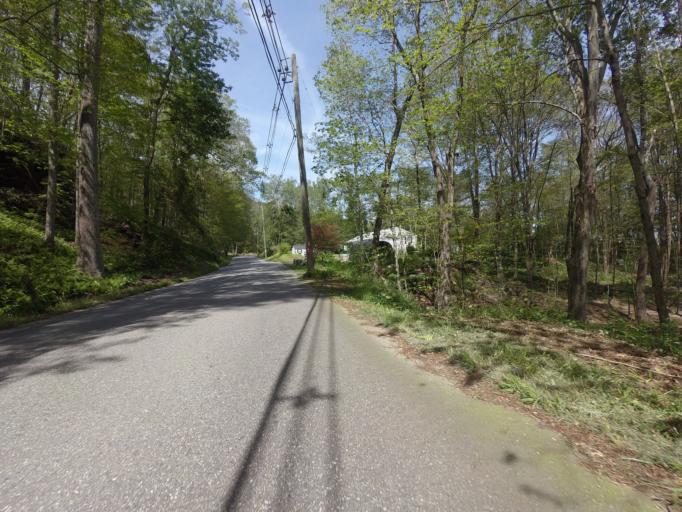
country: US
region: Connecticut
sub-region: Windham County
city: East Brooklyn
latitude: 41.8360
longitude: -71.9356
